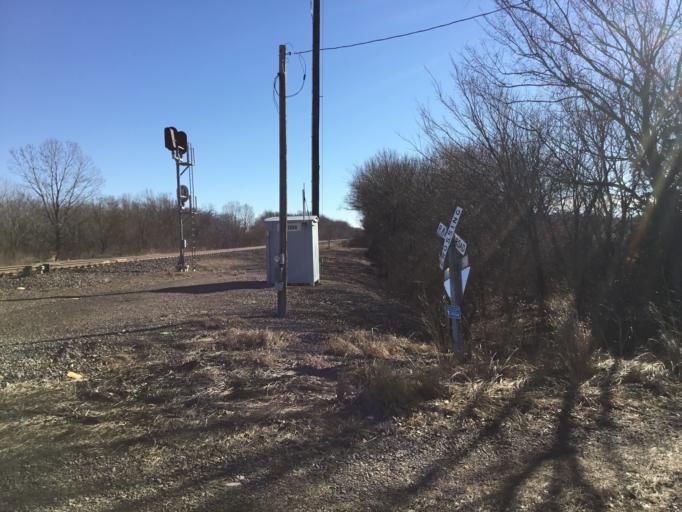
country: US
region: Kansas
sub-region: Shawnee County
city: Silver Lake
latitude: 39.1675
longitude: -95.8592
